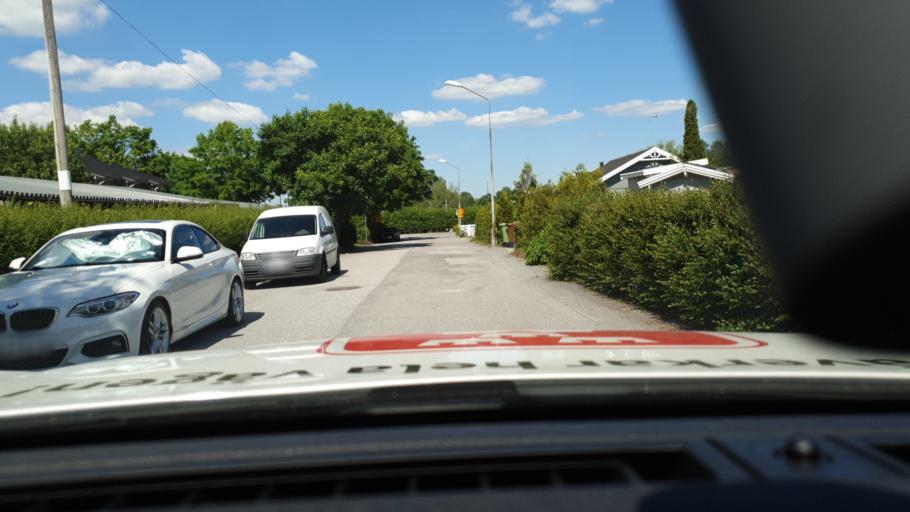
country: SE
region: Stockholm
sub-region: Vallentuna Kommun
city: Vallentuna
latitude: 59.5176
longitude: 18.0647
